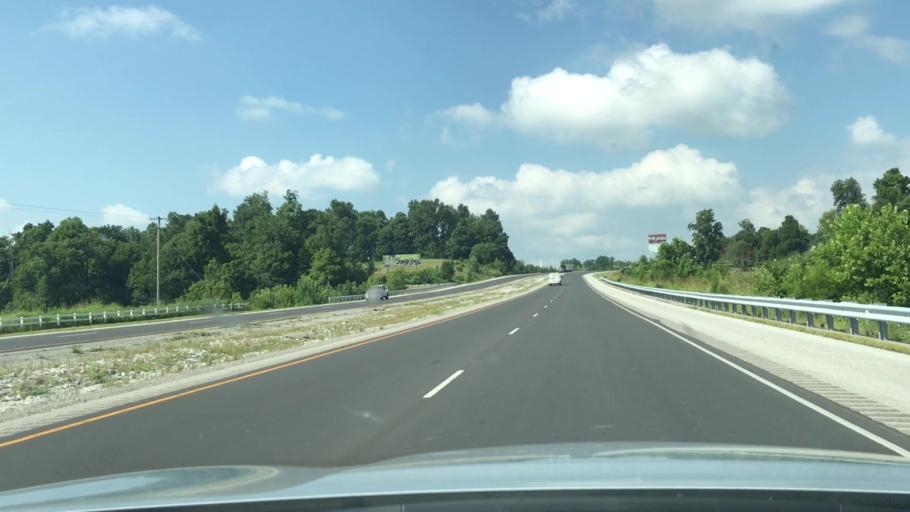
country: US
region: Kentucky
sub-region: Barren County
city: Glasgow
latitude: 37.0188
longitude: -85.9437
